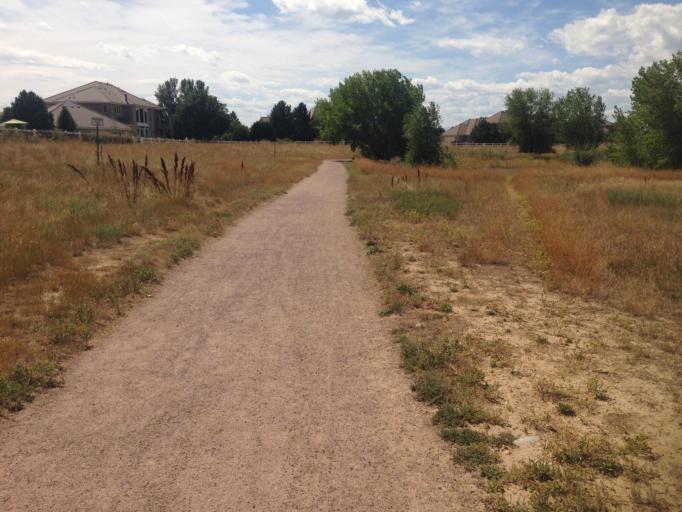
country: US
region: Colorado
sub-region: Adams County
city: Northglenn
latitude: 39.9535
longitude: -105.0078
